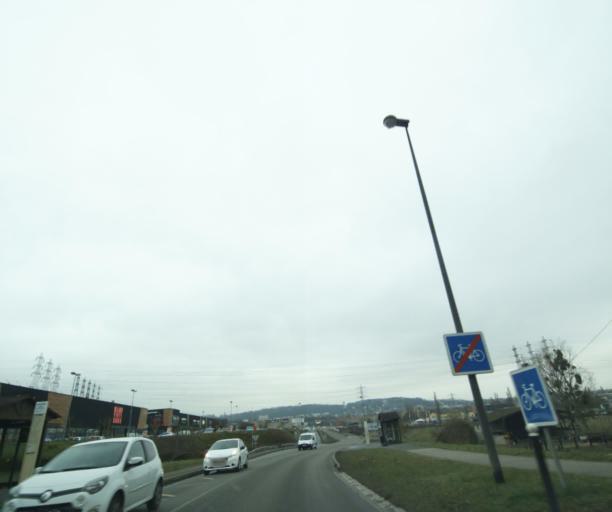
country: FR
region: Ile-de-France
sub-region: Departement de l'Essonne
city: Saulx-les-Chartreux
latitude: 48.7017
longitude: 2.2592
